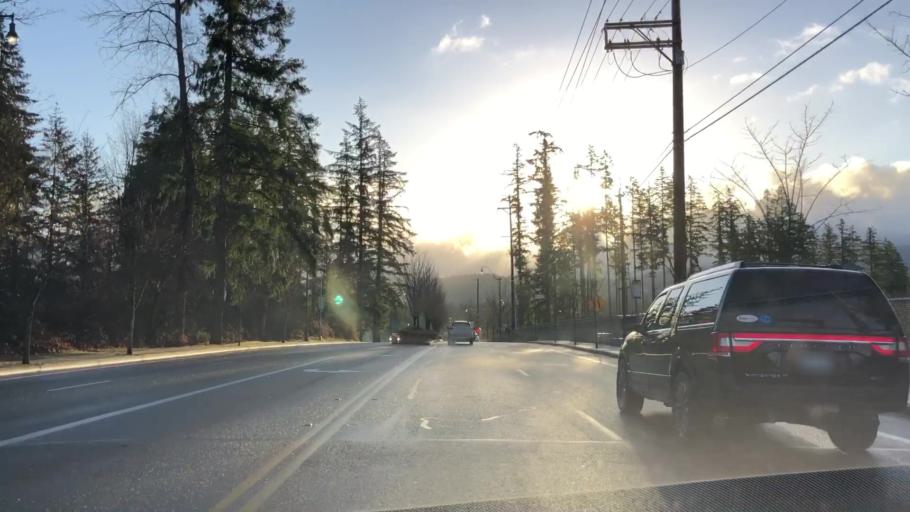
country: US
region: Washington
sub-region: King County
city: City of Sammamish
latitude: 47.5809
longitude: -122.0319
